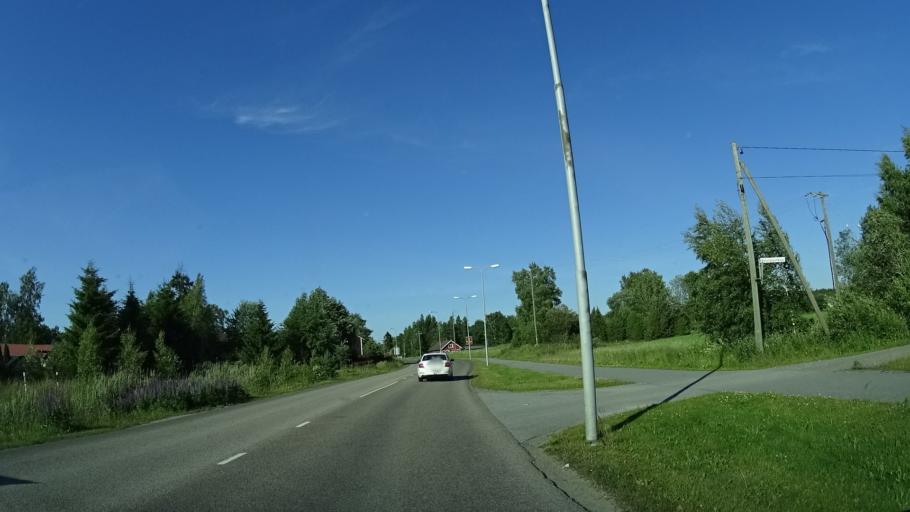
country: FI
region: Satakunta
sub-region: Pori
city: Pori
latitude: 61.5060
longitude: 21.8582
